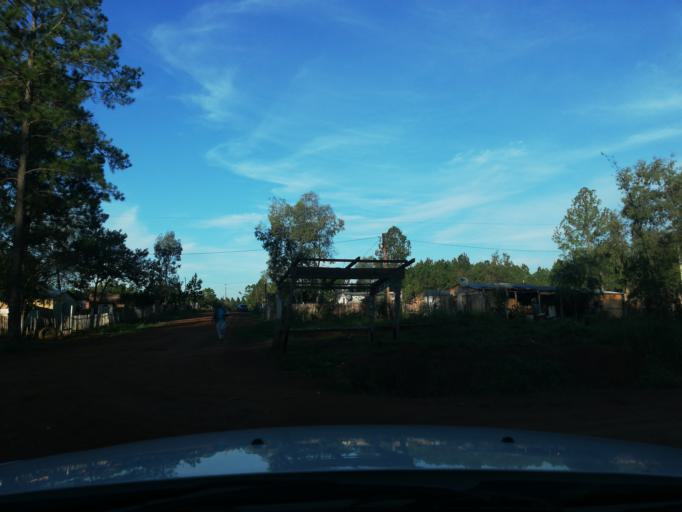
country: AR
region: Misiones
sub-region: Departamento de Capital
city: Posadas
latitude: -27.4776
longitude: -55.9708
